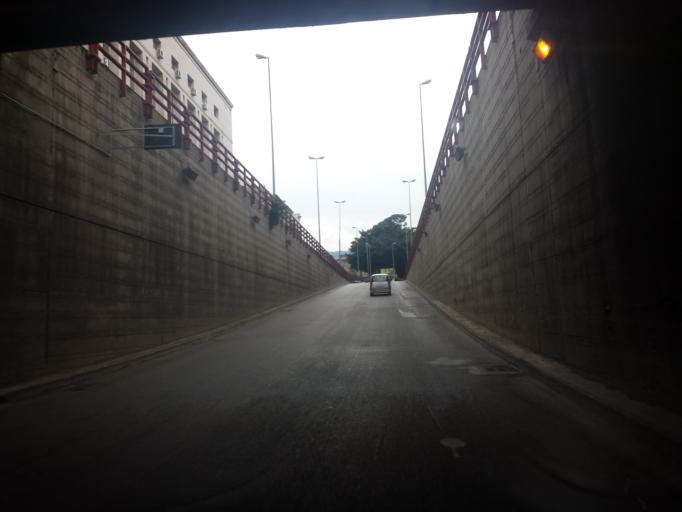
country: IT
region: Sicily
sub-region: Palermo
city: Palermo
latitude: 38.1188
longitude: 13.3509
